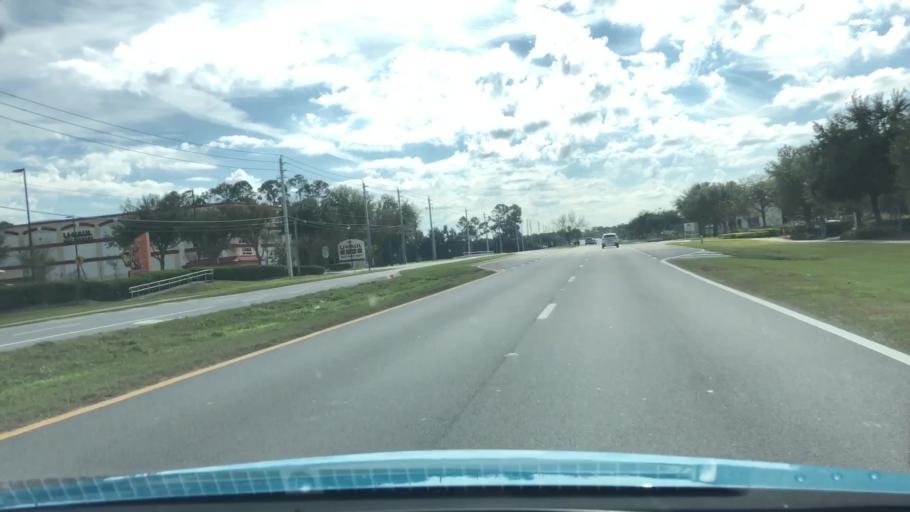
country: US
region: Florida
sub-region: Seminole County
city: Lake Mary
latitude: 28.8093
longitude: -81.3313
